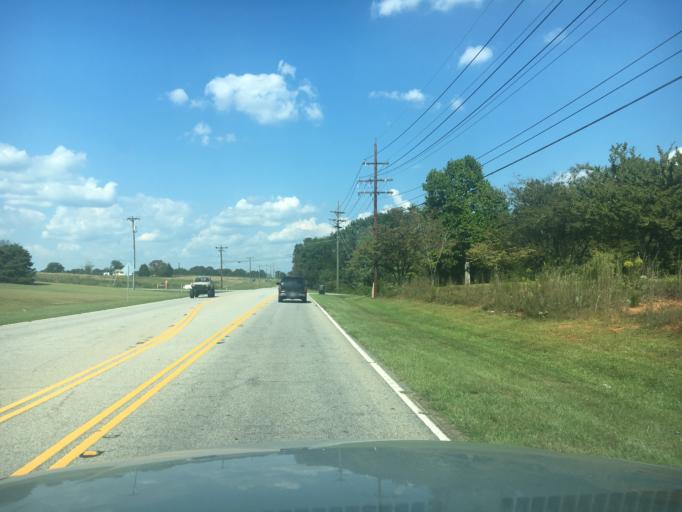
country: US
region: South Carolina
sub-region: Anderson County
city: Pendleton
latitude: 34.5854
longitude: -82.8059
